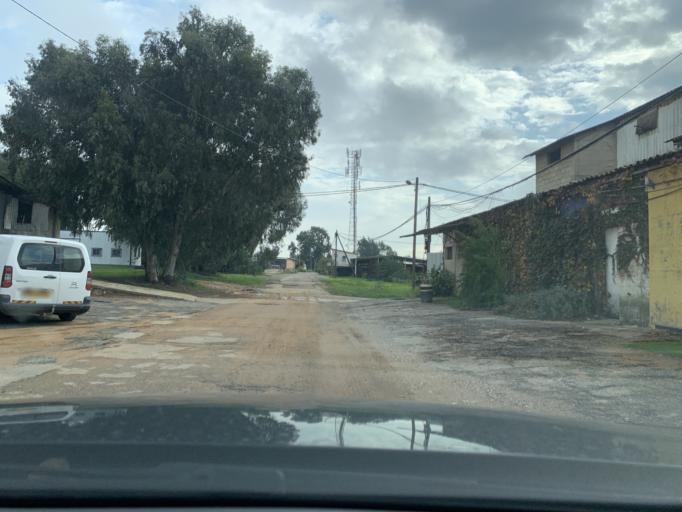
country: PS
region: West Bank
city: Qalqilyah
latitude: 32.1962
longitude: 34.9499
